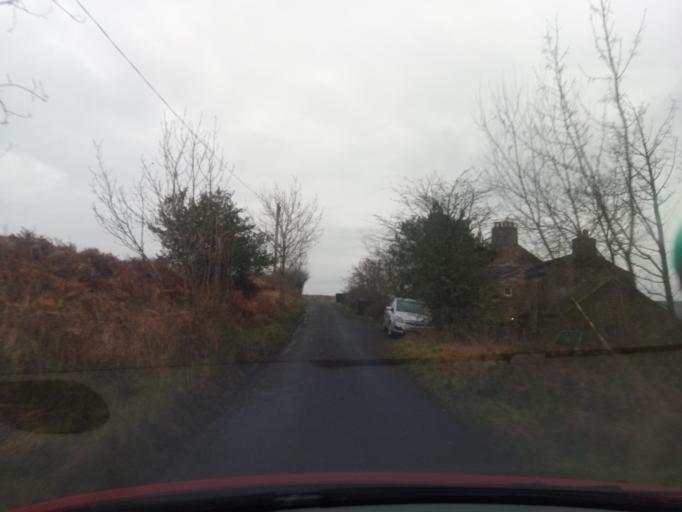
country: GB
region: England
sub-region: Northumberland
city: Rochester
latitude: 55.1756
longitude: -2.4268
